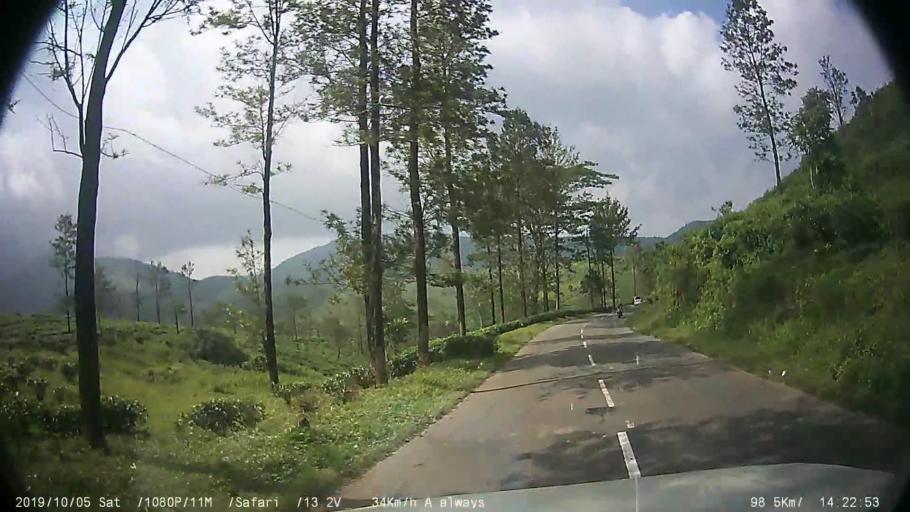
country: IN
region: Kerala
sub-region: Kottayam
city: Erattupetta
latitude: 9.5879
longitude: 76.9666
